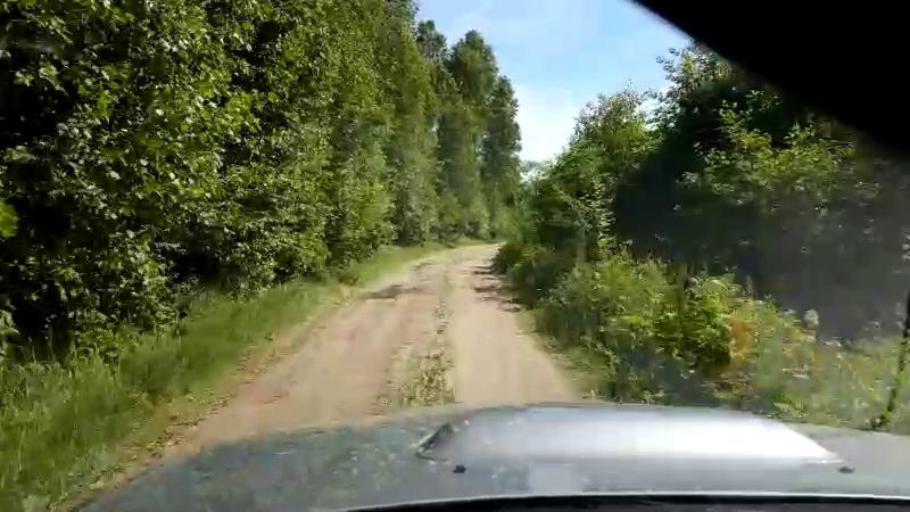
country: EE
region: Paernumaa
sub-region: Sindi linn
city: Sindi
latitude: 58.5329
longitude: 24.6587
